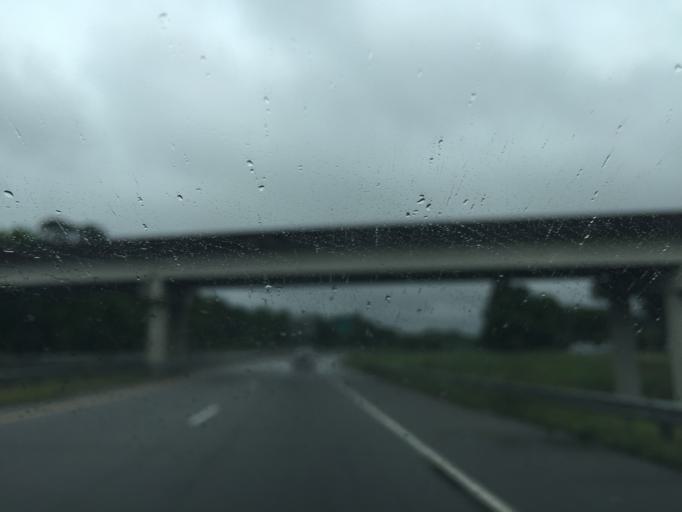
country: US
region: Georgia
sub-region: Chatham County
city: Thunderbolt
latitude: 32.0310
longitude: -81.0848
